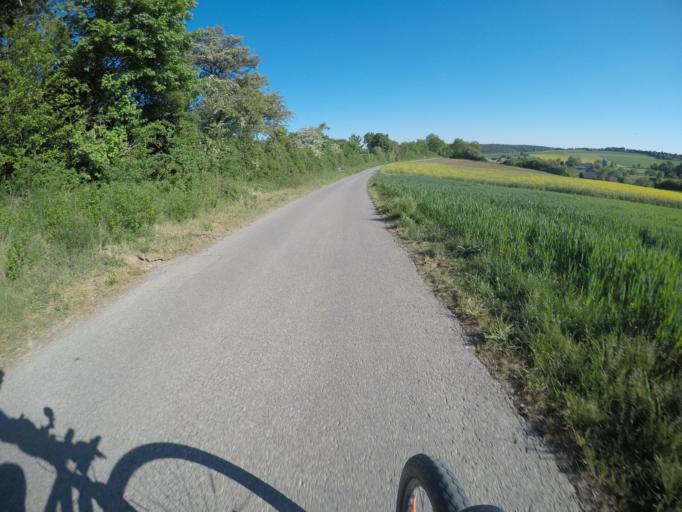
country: DE
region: Baden-Wuerttemberg
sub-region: Regierungsbezirk Stuttgart
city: Weissach
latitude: 48.8553
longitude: 8.9158
